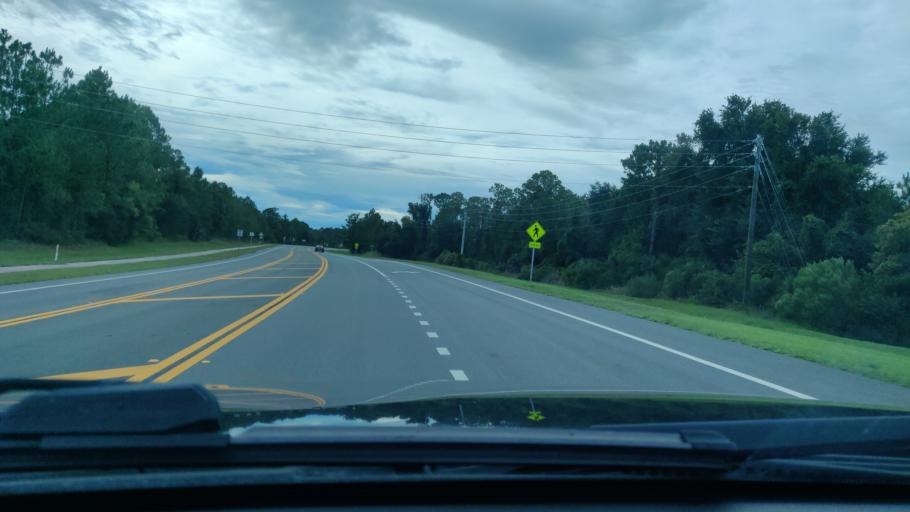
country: US
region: Florida
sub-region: Flagler County
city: Flagler Beach
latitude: 29.5184
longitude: -81.1657
